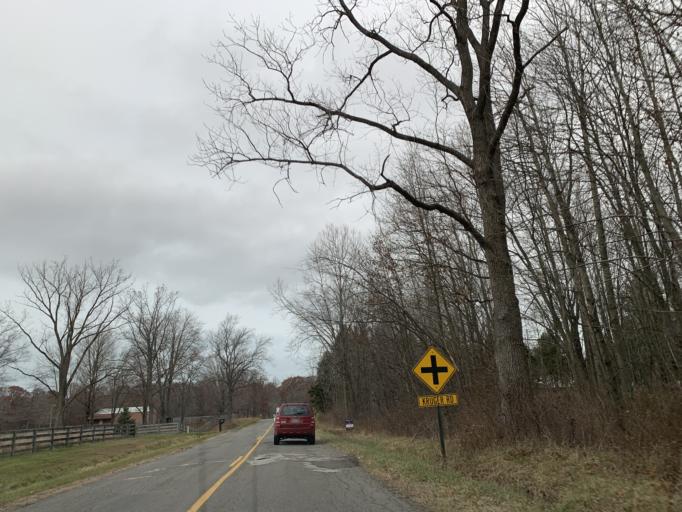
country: US
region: Michigan
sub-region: Berrien County
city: Three Oaks
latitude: 41.8117
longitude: -86.6683
